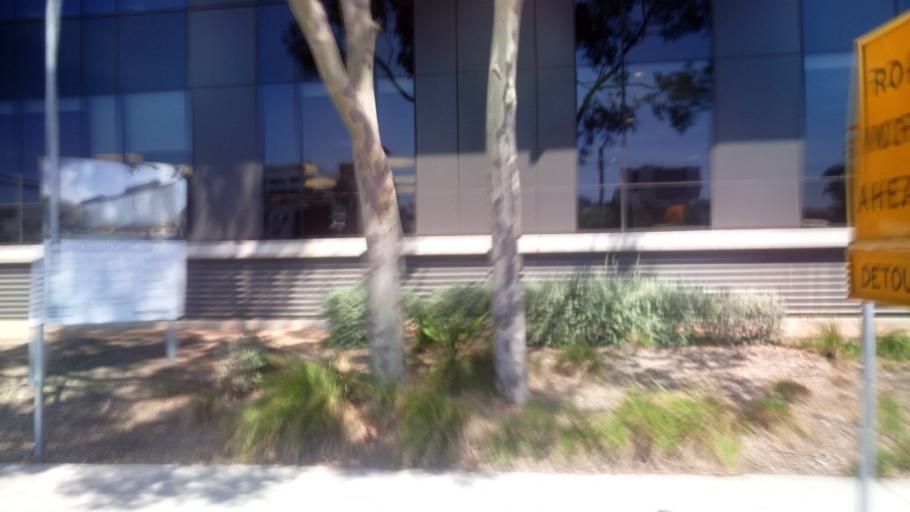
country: AU
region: New South Wales
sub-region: Randwick
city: Kingsford
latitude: -33.9171
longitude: 151.2362
